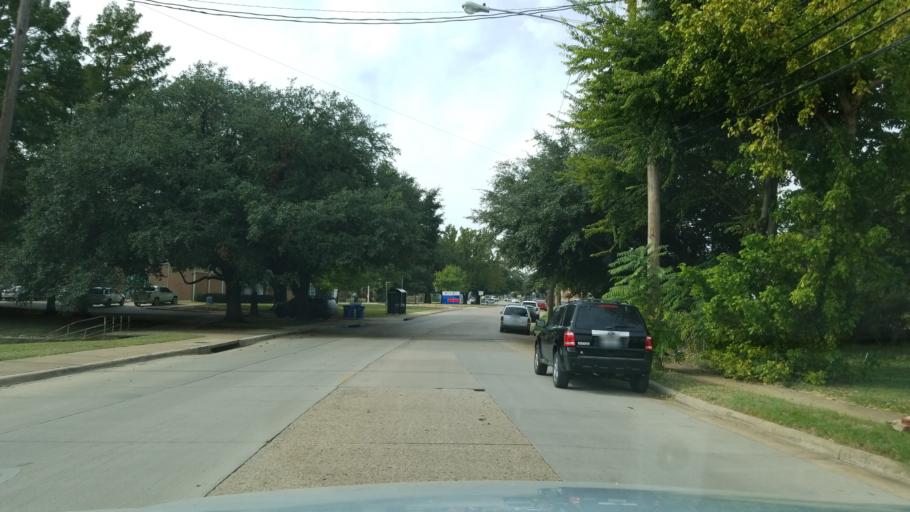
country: US
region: Texas
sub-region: Dallas County
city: Dallas
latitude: 32.7749
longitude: -96.7414
